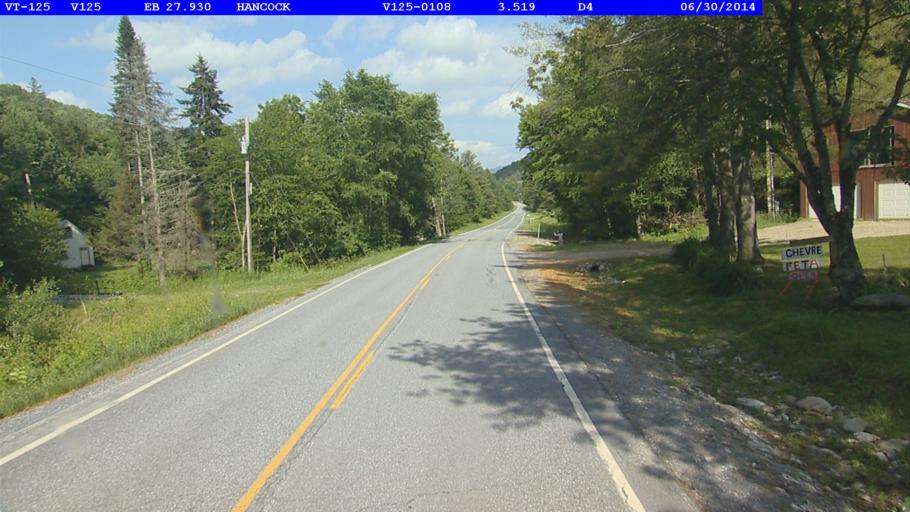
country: US
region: Vermont
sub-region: Rutland County
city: Brandon
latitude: 43.9272
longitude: -72.9122
